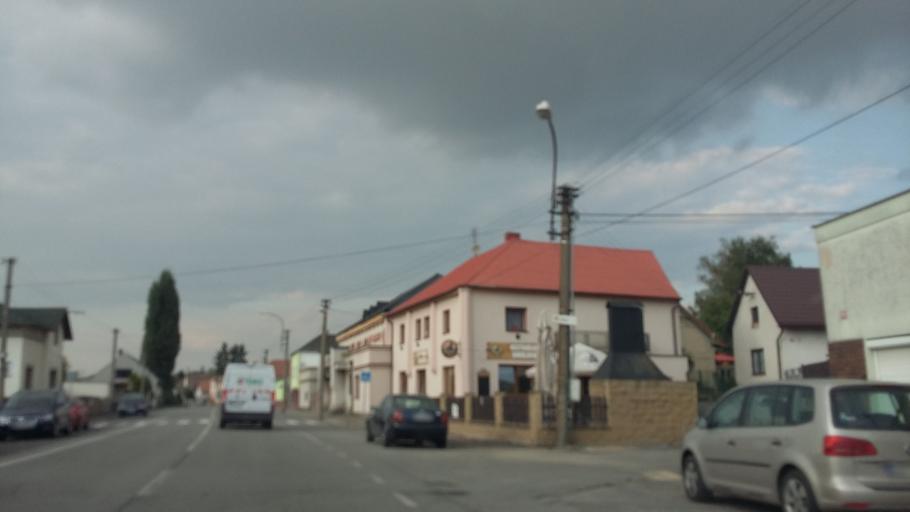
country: CZ
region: Central Bohemia
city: Benatky nad Jizerou
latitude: 50.3272
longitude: 14.8658
